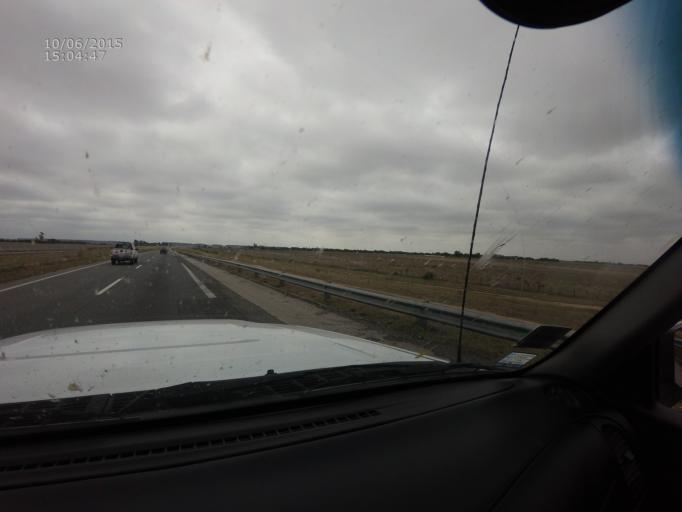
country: AR
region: Cordoba
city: Laguna Larga
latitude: -31.7073
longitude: -63.8140
